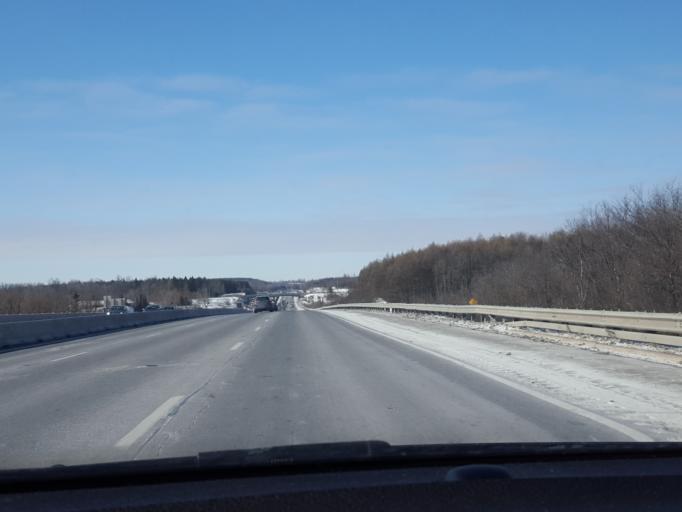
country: CA
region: Ontario
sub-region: Halton
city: Milton
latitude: 43.4800
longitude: -80.0124
